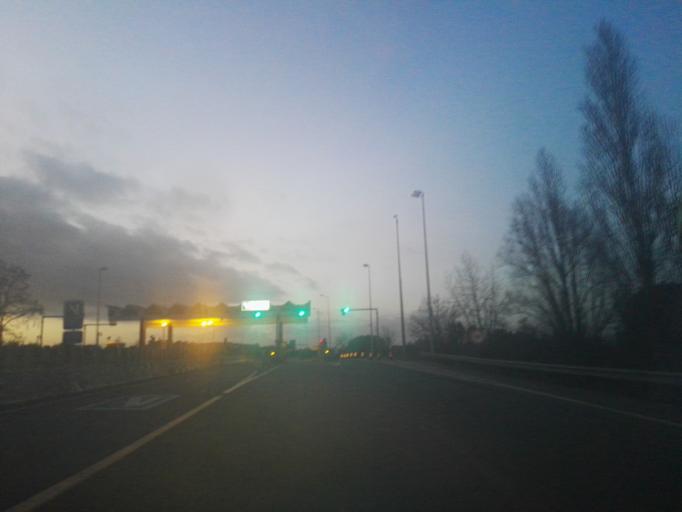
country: PT
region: Evora
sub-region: Montemor-O-Novo
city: Montemor-o-Novo
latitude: 38.6651
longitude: -8.1662
